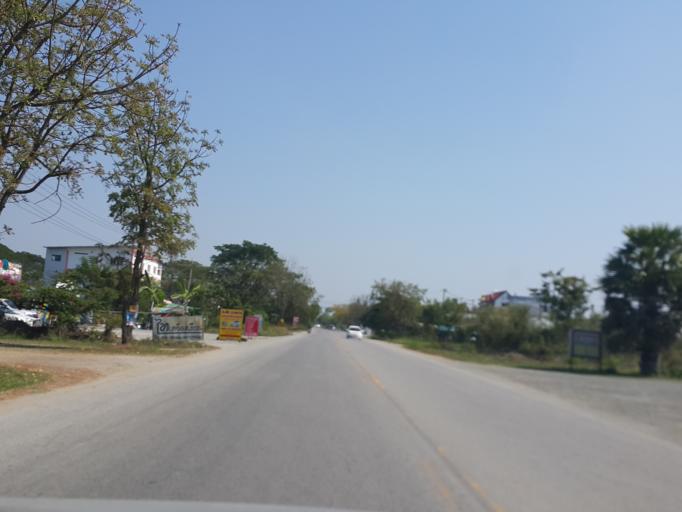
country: TH
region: Chiang Mai
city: San Kamphaeng
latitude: 18.7367
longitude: 99.1211
